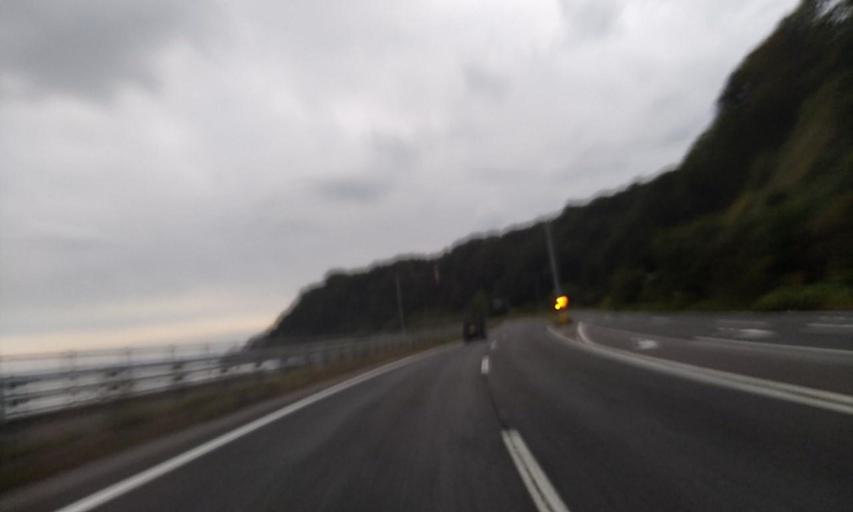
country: JP
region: Hokkaido
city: Abashiri
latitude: 44.0059
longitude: 144.2860
